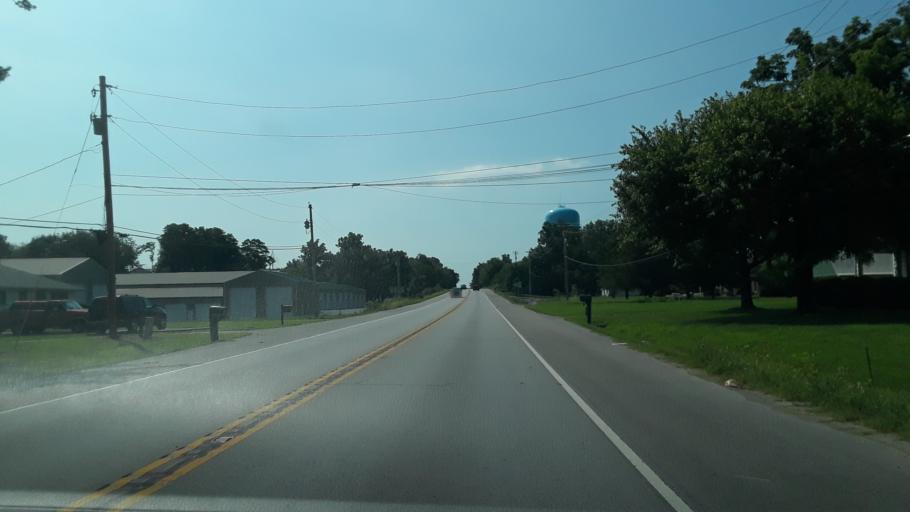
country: US
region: Indiana
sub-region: Clark County
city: Sellersburg
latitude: 38.4236
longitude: -85.8053
